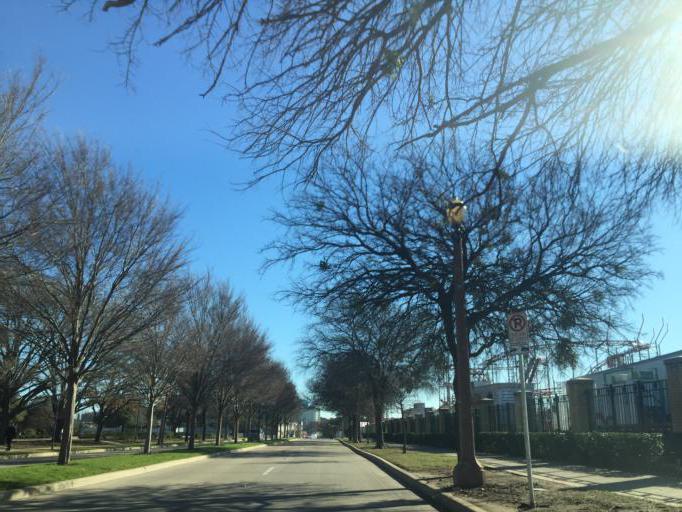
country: US
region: Texas
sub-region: Tarrant County
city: River Oaks
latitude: 32.7474
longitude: -97.3644
